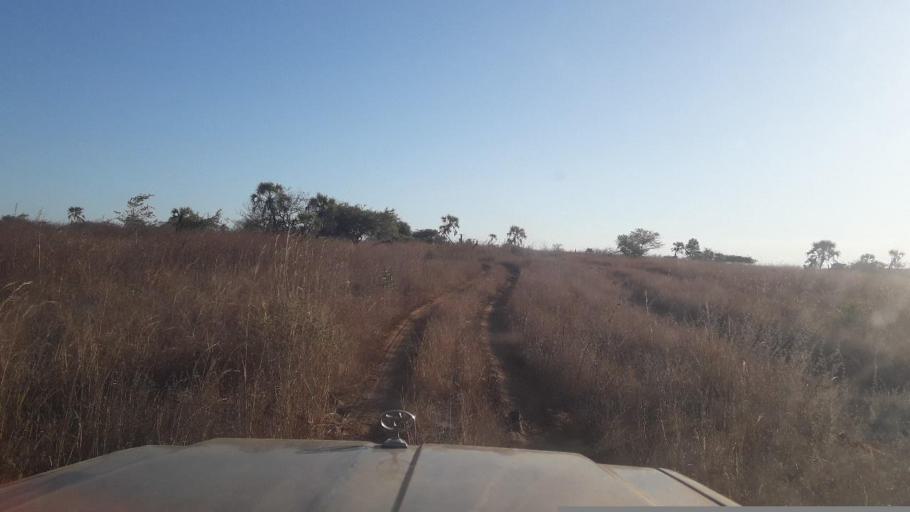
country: MG
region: Boeny
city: Sitampiky
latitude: -16.4985
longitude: 45.6055
